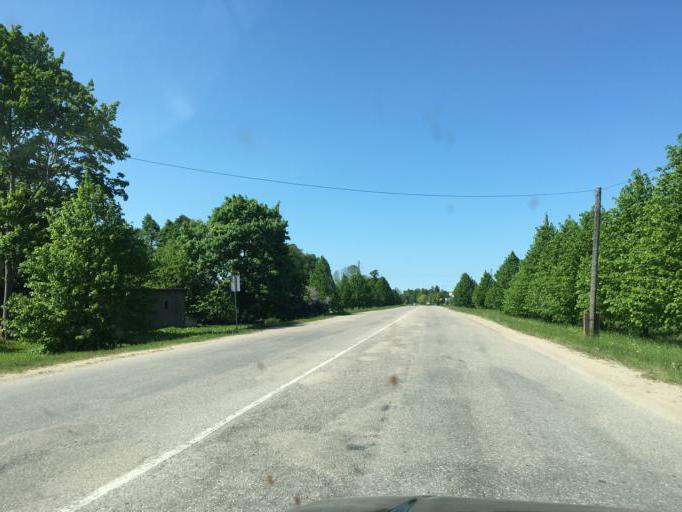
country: LV
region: Dundaga
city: Dundaga
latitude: 57.5004
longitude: 22.3529
